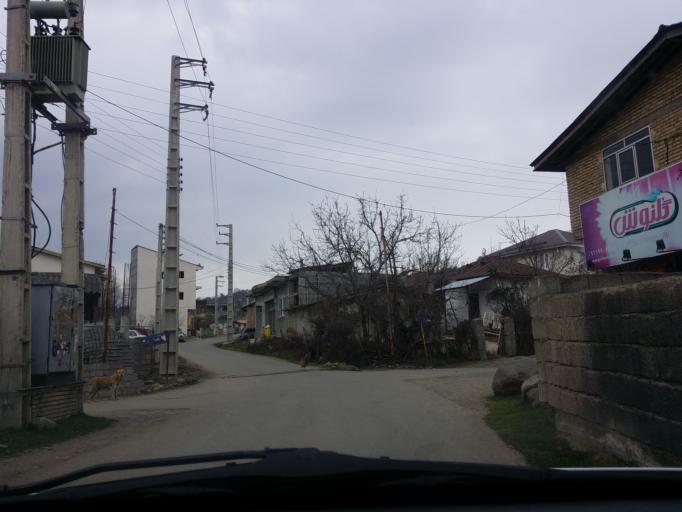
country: IR
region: Mazandaran
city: `Abbasabad
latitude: 36.5479
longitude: 51.1664
